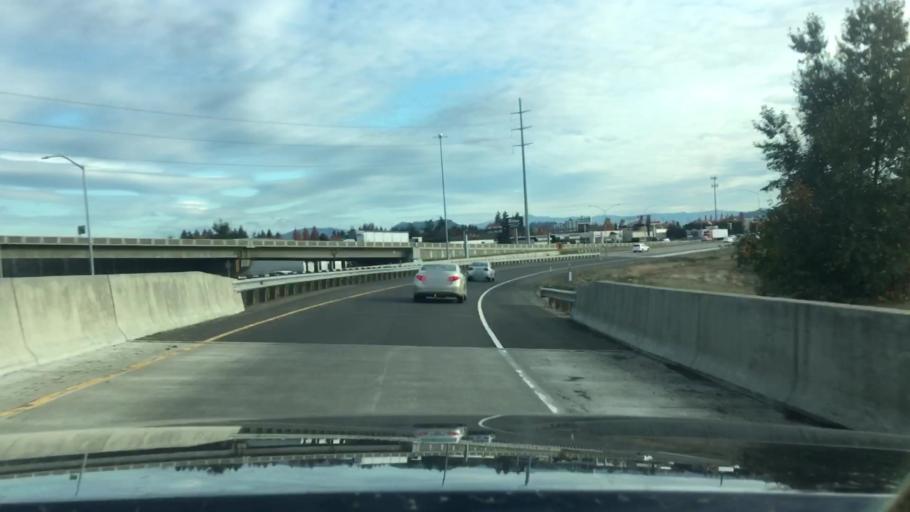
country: US
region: Oregon
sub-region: Lane County
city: Springfield
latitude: 44.0825
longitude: -123.0483
